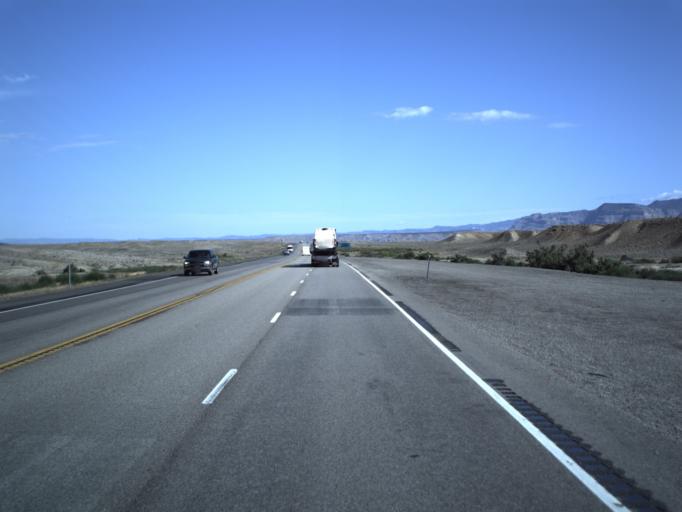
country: US
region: Utah
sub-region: Carbon County
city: East Carbon City
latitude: 39.2925
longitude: -110.3532
